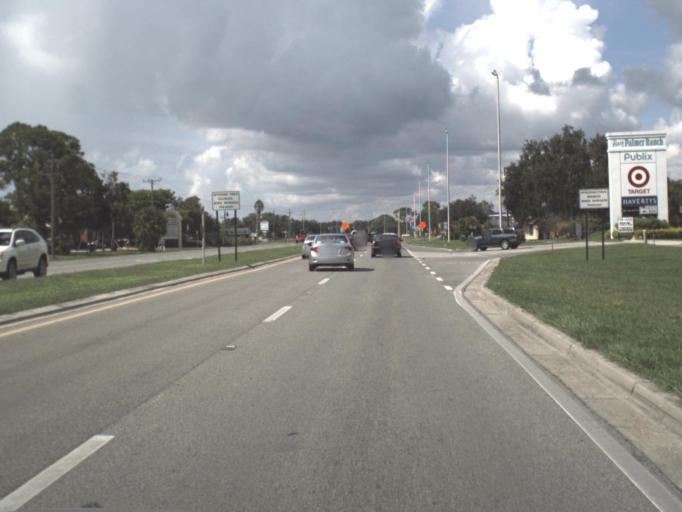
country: US
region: Florida
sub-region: Sarasota County
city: Vamo
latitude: 27.2261
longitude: -82.4932
